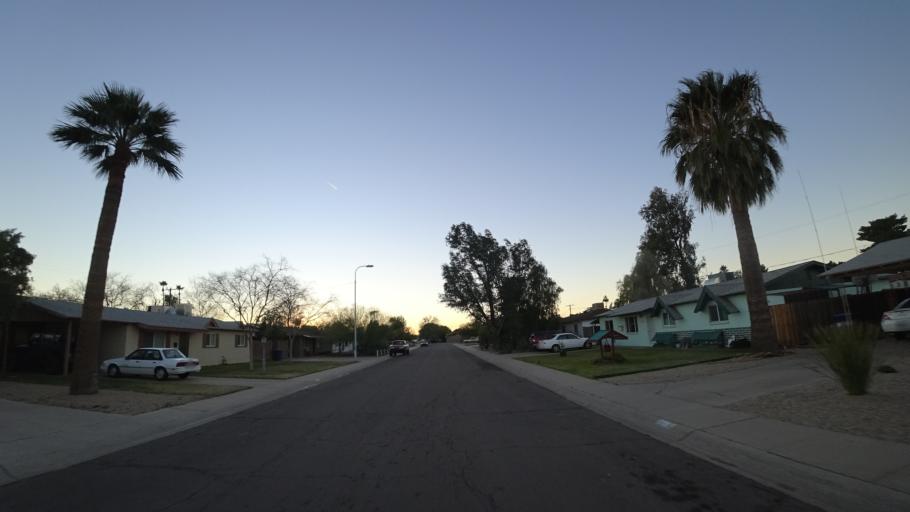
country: US
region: Arizona
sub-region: Maricopa County
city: Tempe Junction
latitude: 33.4197
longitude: -111.9551
